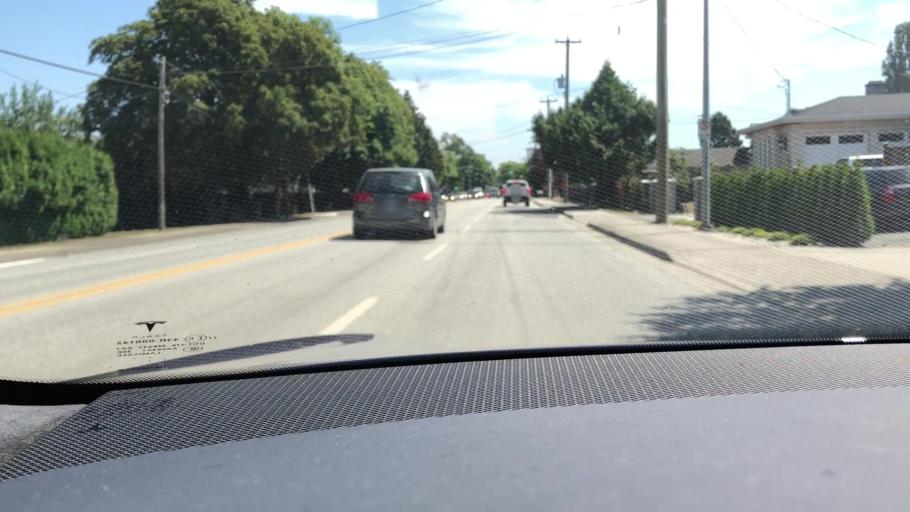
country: CA
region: British Columbia
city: Richmond
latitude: 49.1845
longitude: -123.0996
